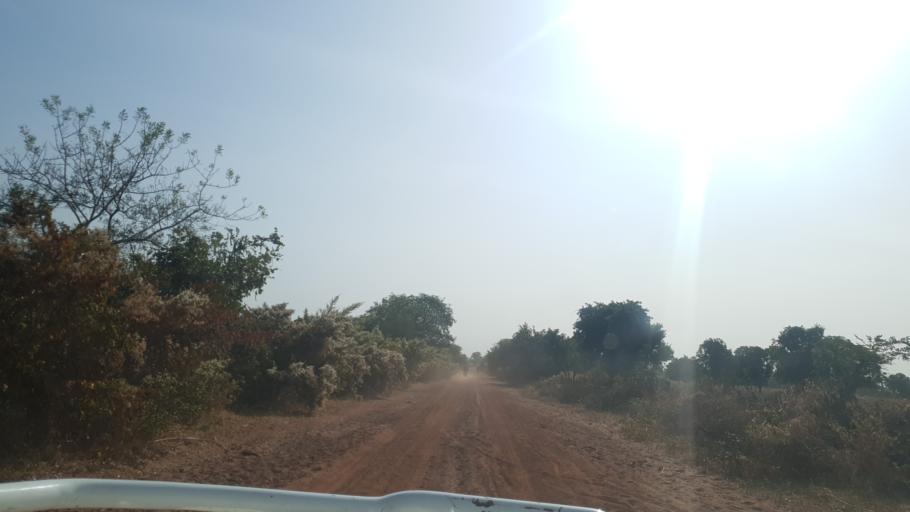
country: ML
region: Koulikoro
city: Dioila
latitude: 12.7091
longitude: -6.7817
